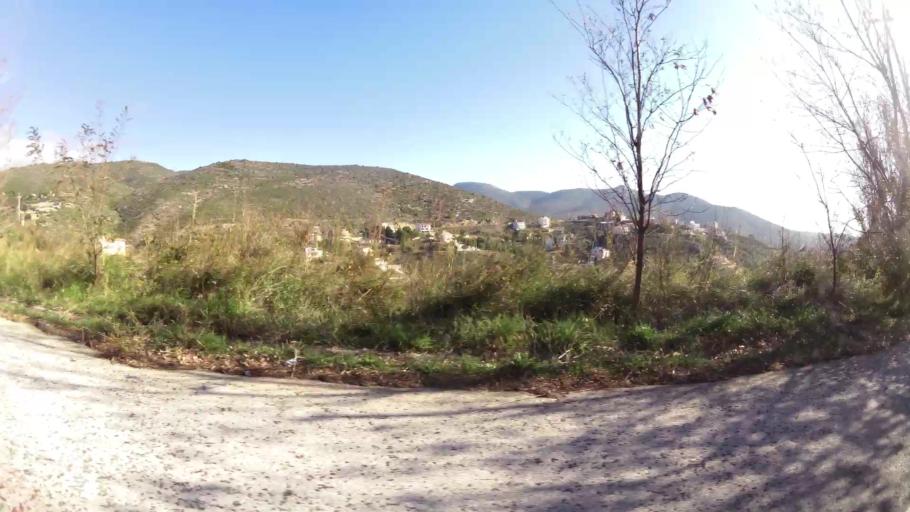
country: GR
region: Attica
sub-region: Nomarchia Anatolikis Attikis
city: Dhrafi
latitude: 38.0420
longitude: 23.8940
